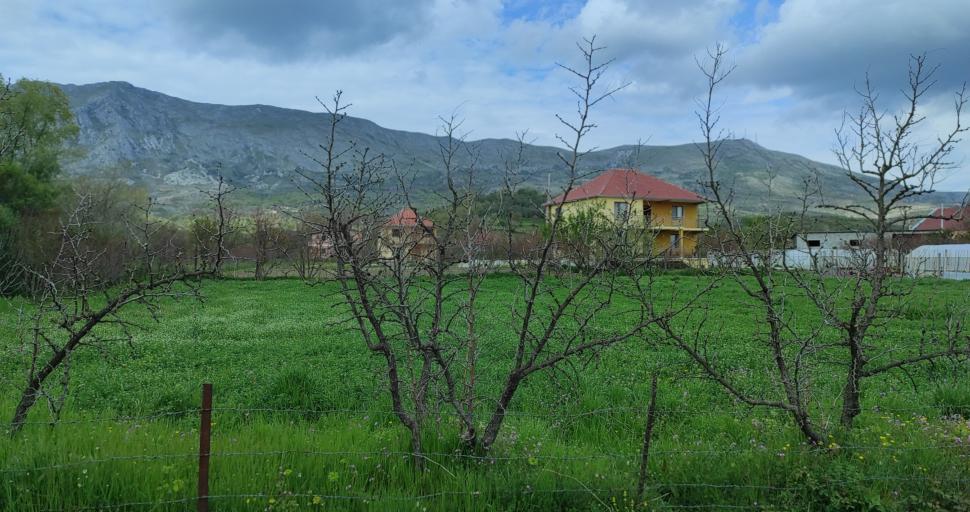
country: AL
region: Shkoder
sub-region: Rrethi i Shkodres
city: Dajc
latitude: 42.0327
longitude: 19.4132
